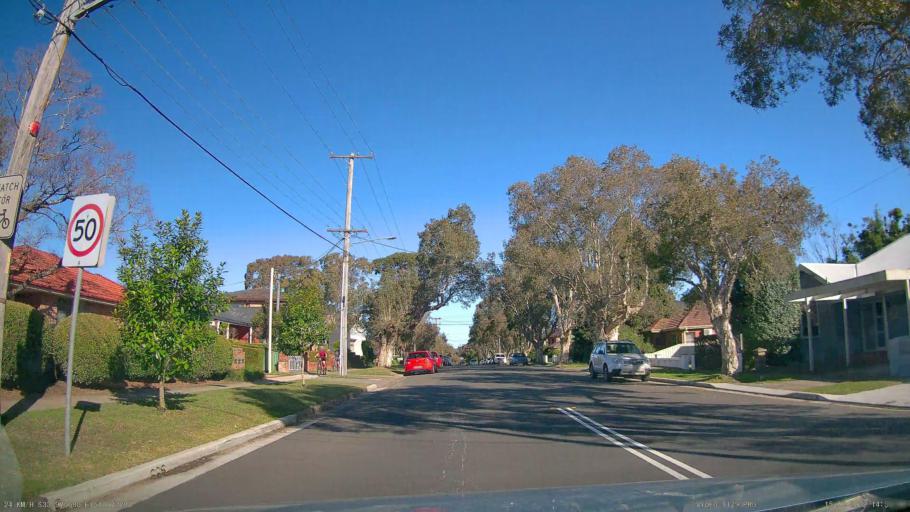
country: AU
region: New South Wales
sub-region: Hurstville
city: Oatley
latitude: -33.9758
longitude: 151.0722
